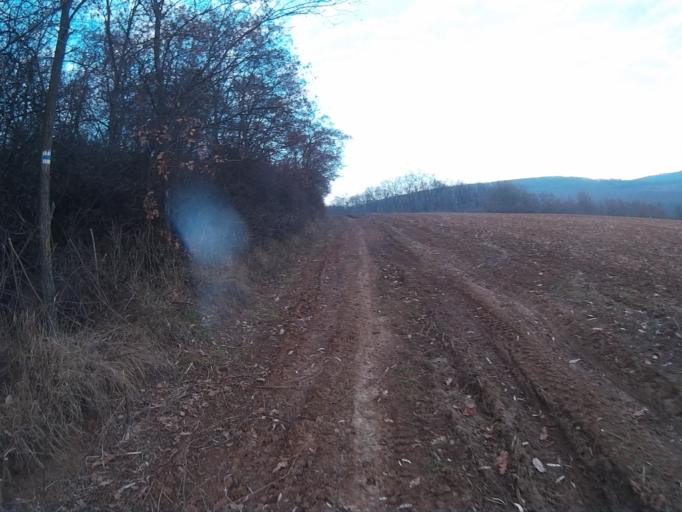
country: HU
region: Nograd
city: Rimoc
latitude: 47.9943
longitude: 19.4304
